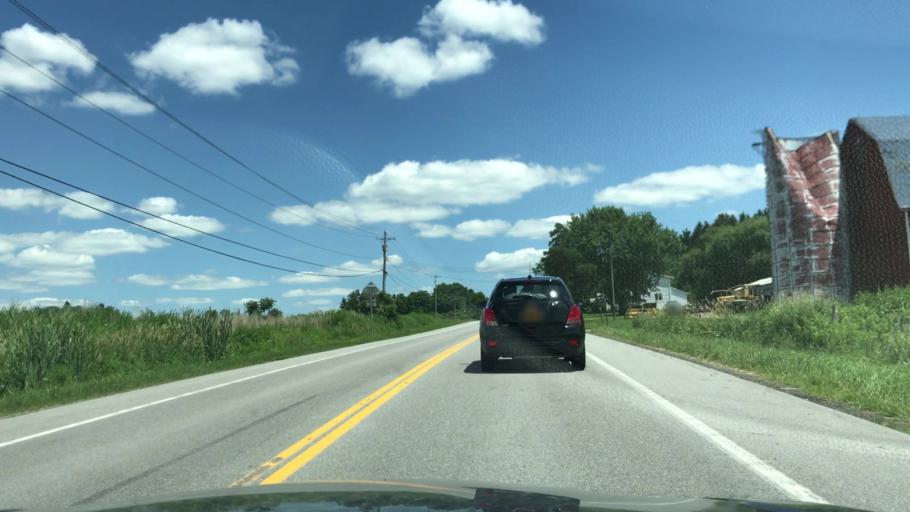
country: US
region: New York
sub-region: Wyoming County
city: Attica
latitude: 42.7705
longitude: -78.3621
